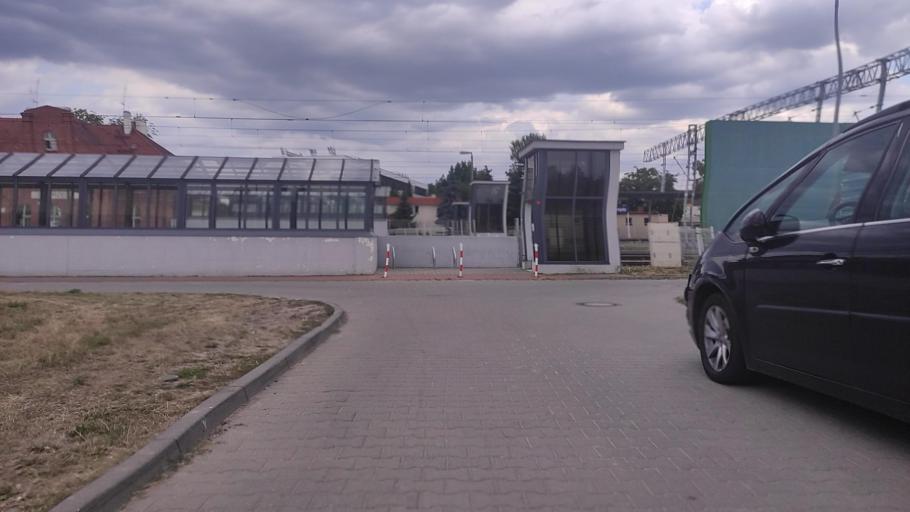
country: PL
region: Greater Poland Voivodeship
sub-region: Powiat poznanski
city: Swarzedz
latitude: 52.4039
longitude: 17.0751
